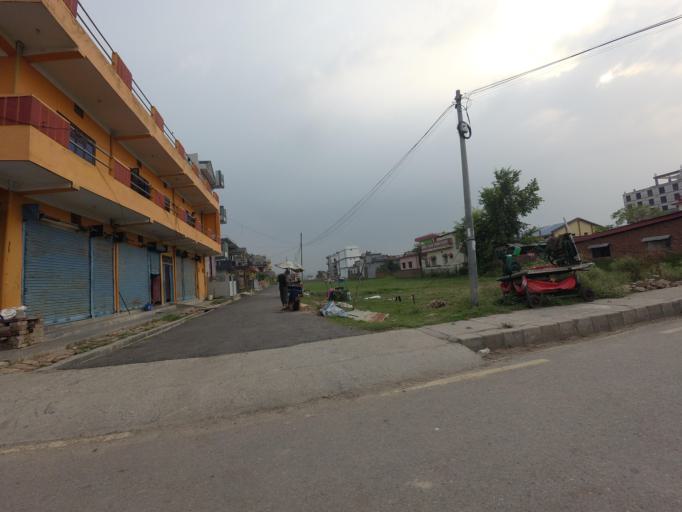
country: NP
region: Western Region
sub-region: Lumbini Zone
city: Bhairahawa
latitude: 27.5193
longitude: 83.4459
